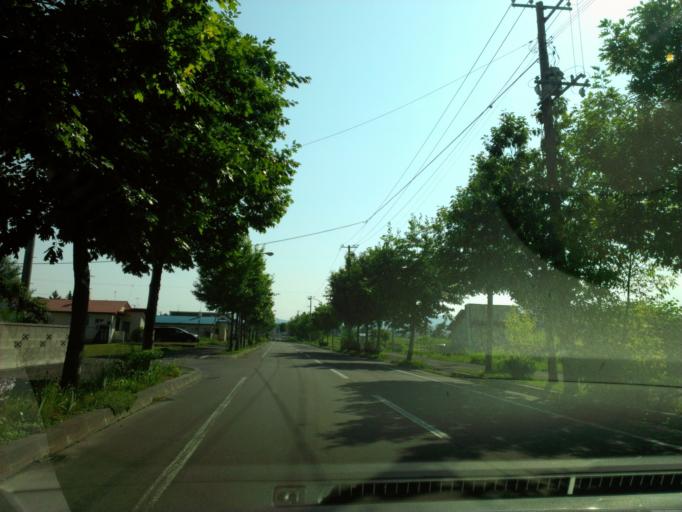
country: JP
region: Hokkaido
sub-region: Asahikawa-shi
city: Asahikawa
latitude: 43.5971
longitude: 142.4707
